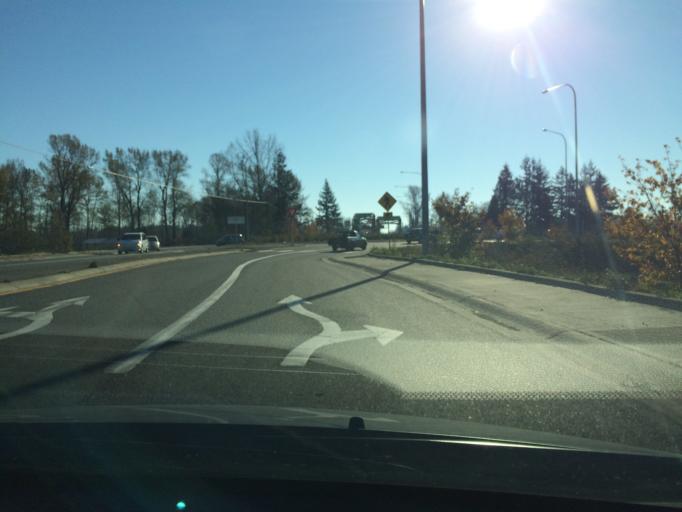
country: US
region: Washington
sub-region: Whatcom County
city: Lynden
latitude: 48.9235
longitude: -122.4858
